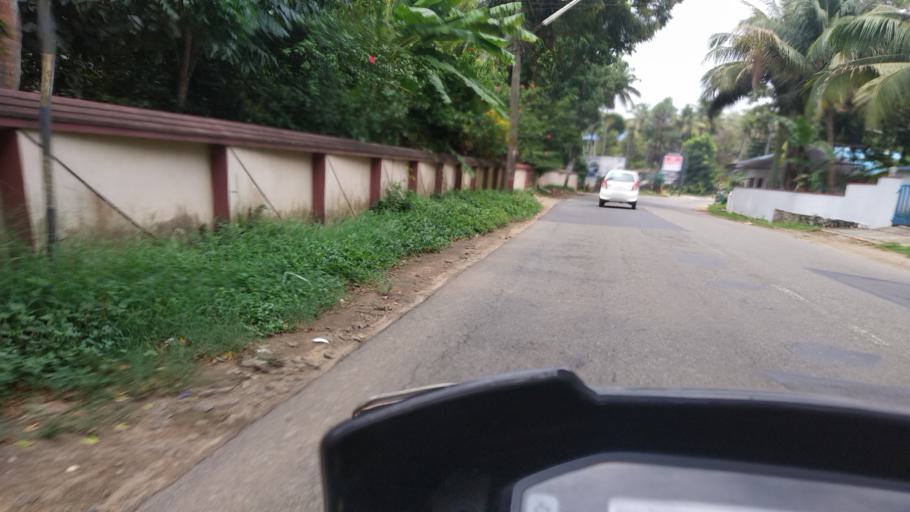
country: IN
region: Kerala
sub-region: Ernakulam
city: Perumpavur
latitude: 10.1103
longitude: 76.5340
